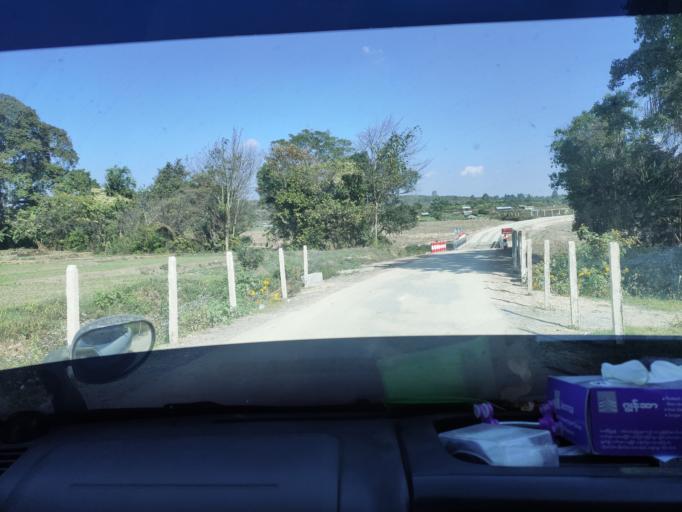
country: MM
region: Mandalay
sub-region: Pyin Oo Lwin District
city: Pyin Oo Lwin
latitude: 22.0655
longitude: 96.5306
